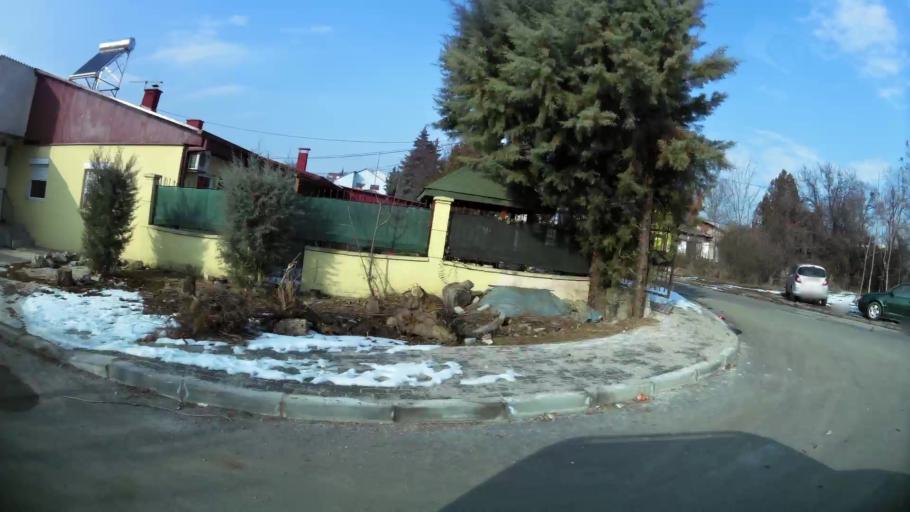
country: MK
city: Creshevo
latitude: 42.0047
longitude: 21.4962
